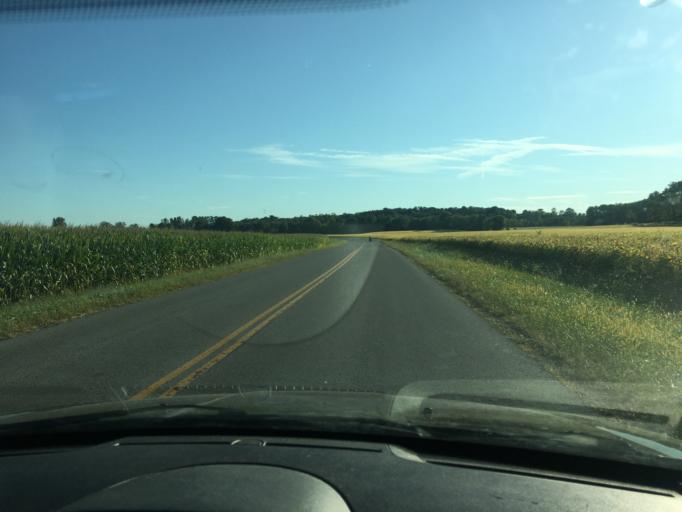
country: US
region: Ohio
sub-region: Logan County
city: West Liberty
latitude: 40.3017
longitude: -83.7109
